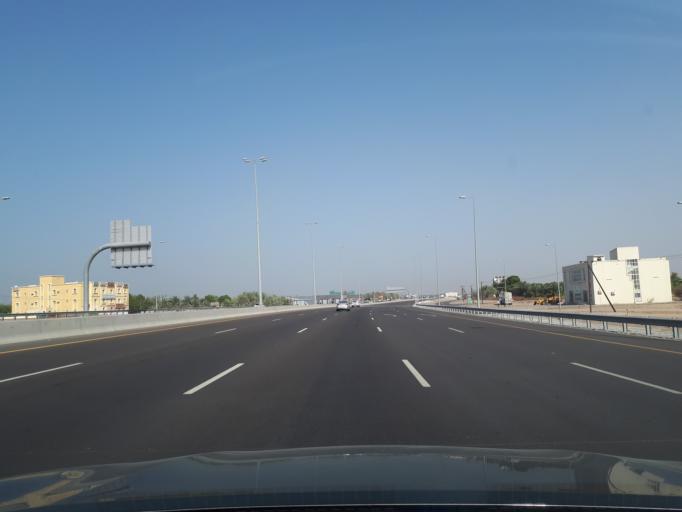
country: OM
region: Al Batinah
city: Al Liwa'
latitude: 24.4192
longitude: 56.6236
